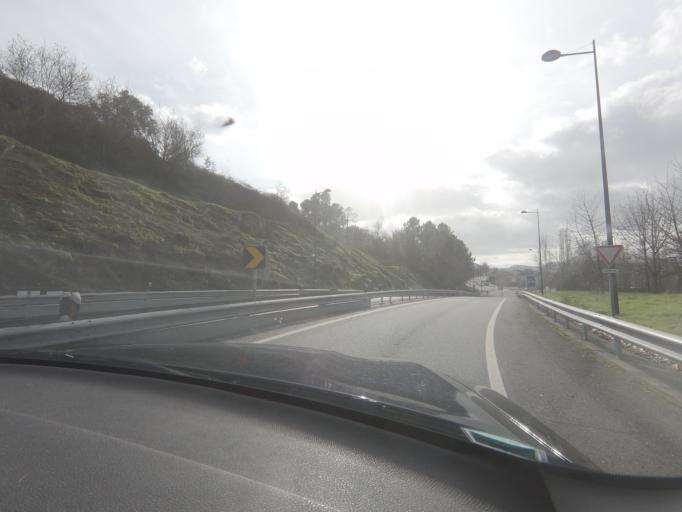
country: PT
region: Vila Real
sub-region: Vila Real
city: Vila Real
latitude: 41.3044
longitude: -7.7504
